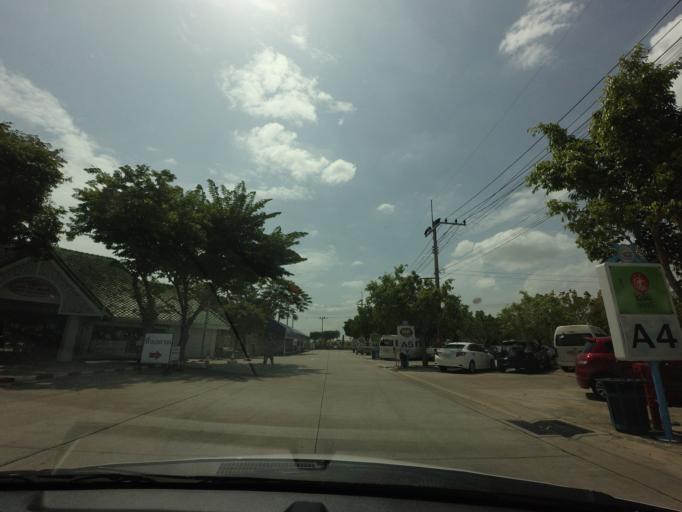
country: TH
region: Pathum Thani
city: Thanyaburi
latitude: 13.9873
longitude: 100.6749
